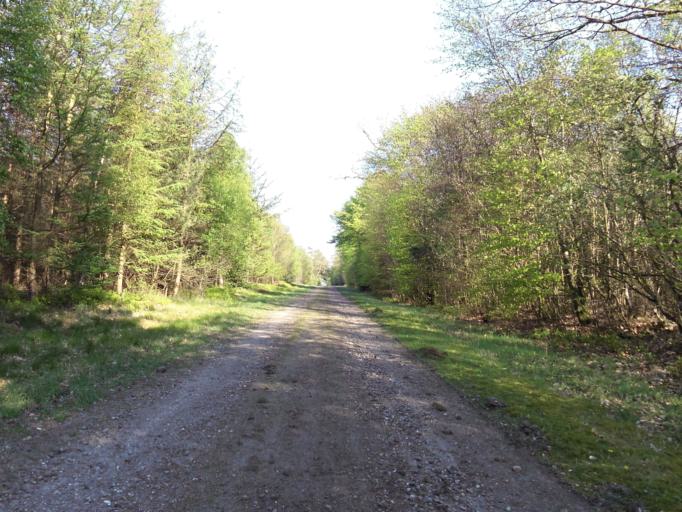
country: DK
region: South Denmark
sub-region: Tonder Kommune
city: Toftlund
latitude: 55.1933
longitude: 8.9542
